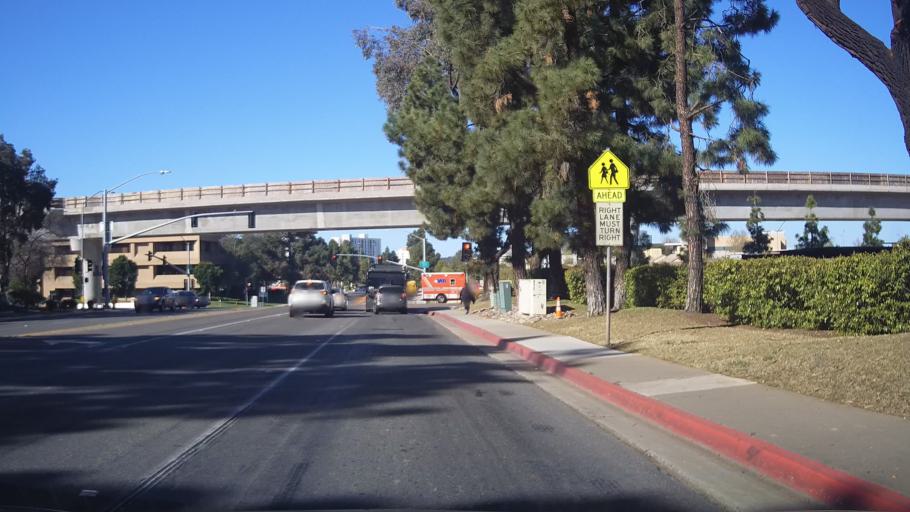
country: US
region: California
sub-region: San Diego County
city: La Jolla
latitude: 32.8779
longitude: -117.2132
